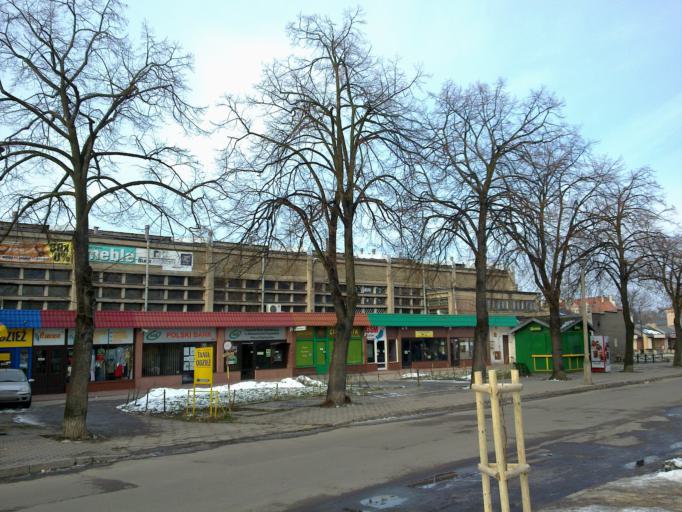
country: PL
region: Kujawsko-Pomorskie
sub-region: Powiat aleksandrowski
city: Ciechocinek
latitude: 52.8788
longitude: 18.7872
